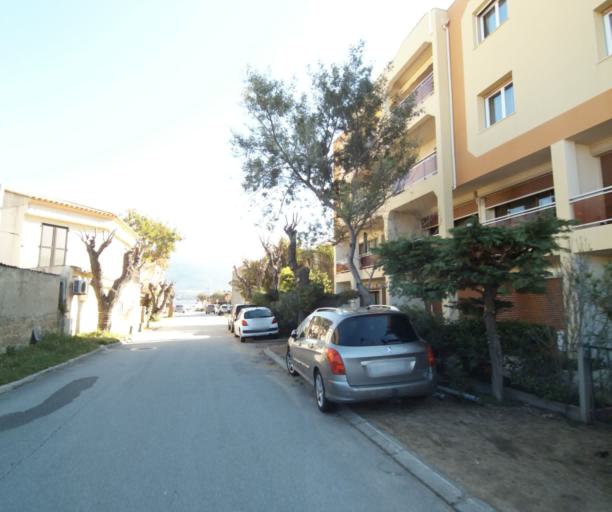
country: FR
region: Corsica
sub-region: Departement de la Corse-du-Sud
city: Propriano
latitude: 41.6748
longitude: 8.8984
